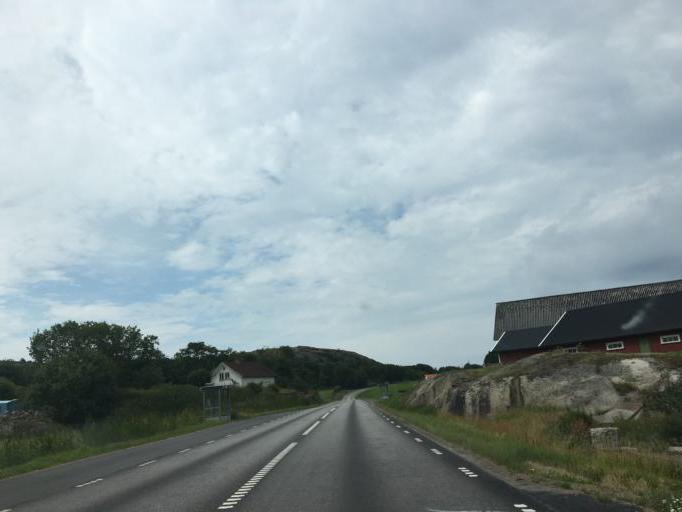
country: SE
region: Vaestra Goetaland
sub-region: Sotenas Kommun
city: Hunnebostrand
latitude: 58.4161
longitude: 11.2868
